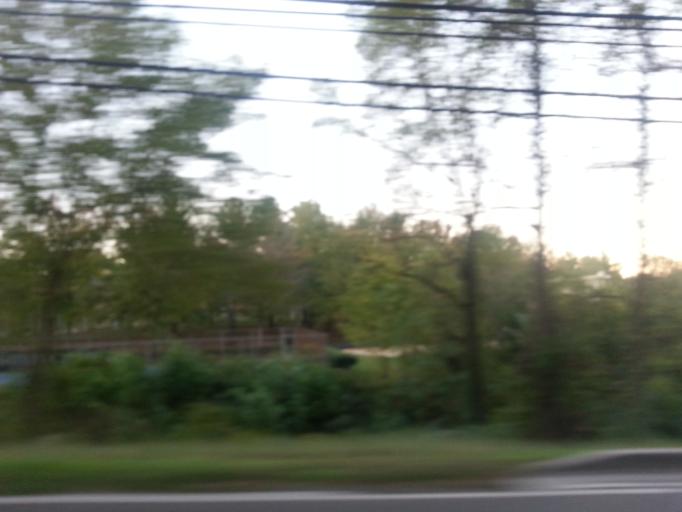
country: US
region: Tennessee
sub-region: Knox County
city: Knoxville
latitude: 36.0159
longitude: -83.9782
